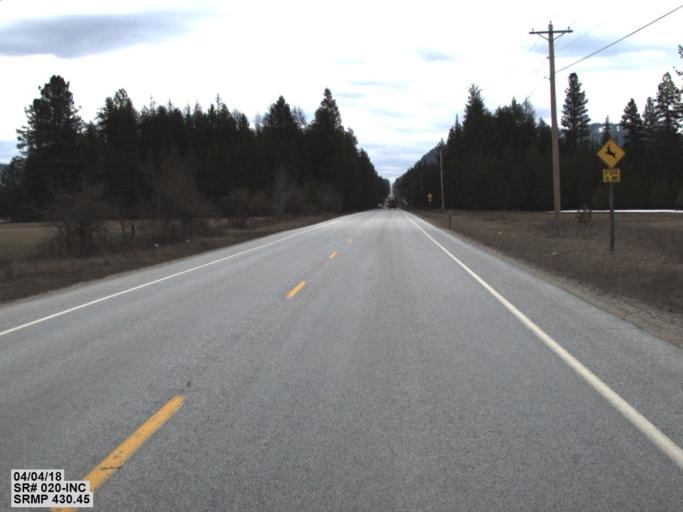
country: US
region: Washington
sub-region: Pend Oreille County
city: Newport
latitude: 48.2290
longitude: -117.1525
